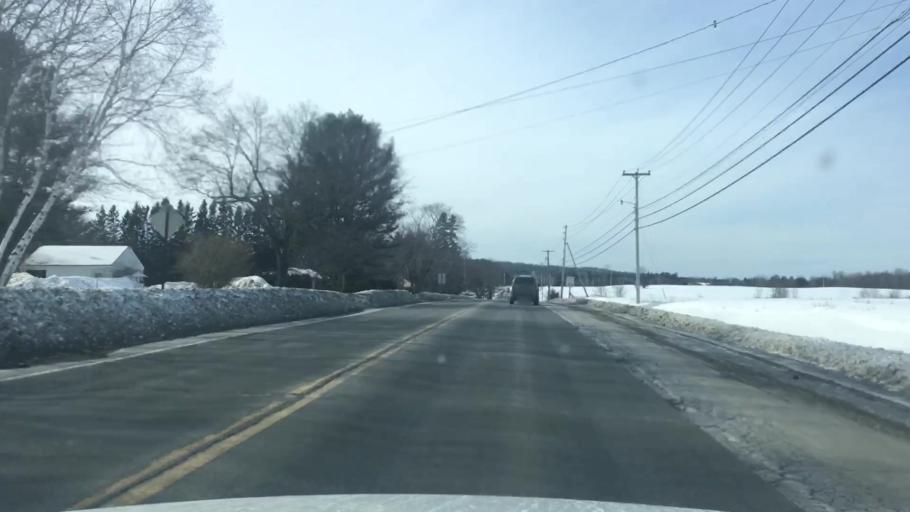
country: US
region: Maine
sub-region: Penobscot County
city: Bangor
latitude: 44.8534
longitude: -68.8122
